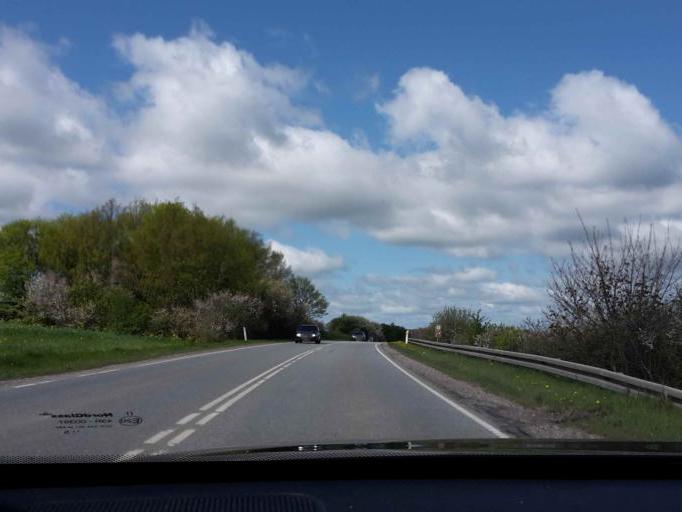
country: DK
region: Central Jutland
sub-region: Arhus Kommune
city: Logten
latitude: 56.2879
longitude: 10.3149
